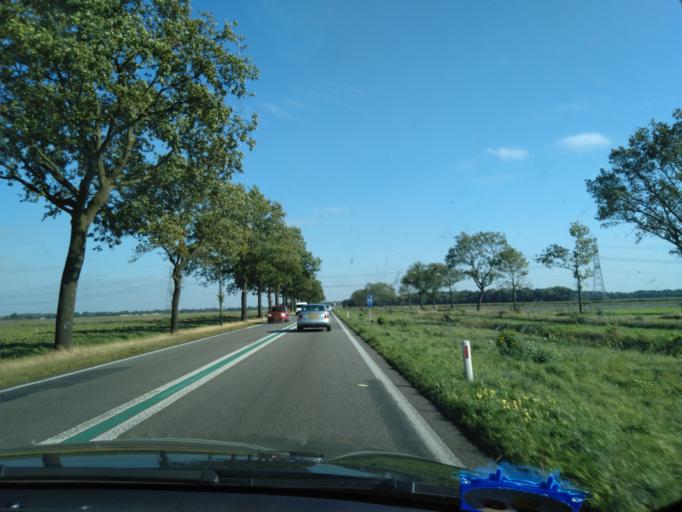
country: NL
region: Groningen
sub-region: Gemeente Veendam
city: Veendam
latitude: 53.0899
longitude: 6.9416
